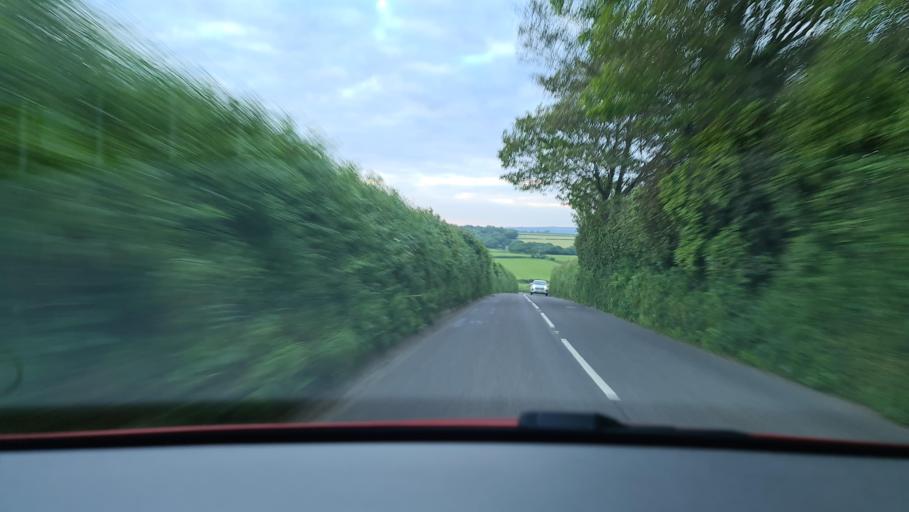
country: GB
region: England
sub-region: Cornwall
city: Looe
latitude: 50.4097
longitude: -4.4252
